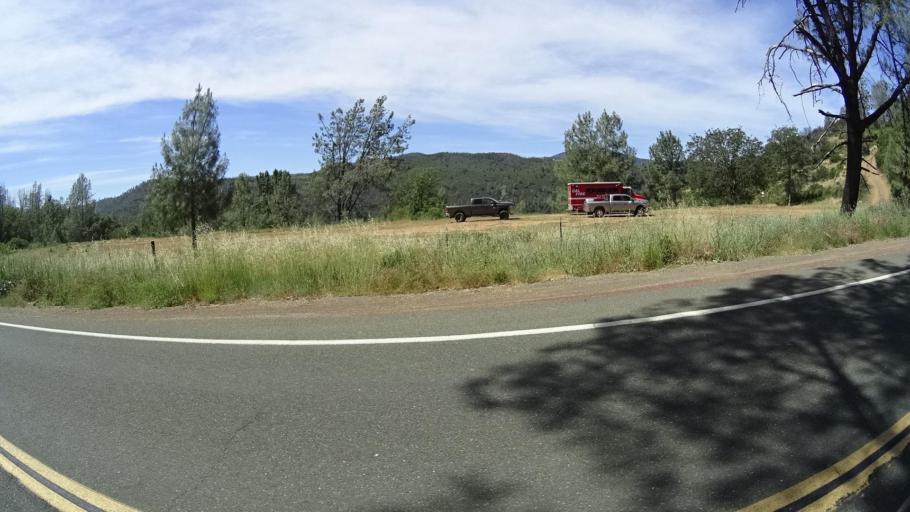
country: US
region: California
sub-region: Lake County
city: Clearlake
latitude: 38.9365
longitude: -122.6652
